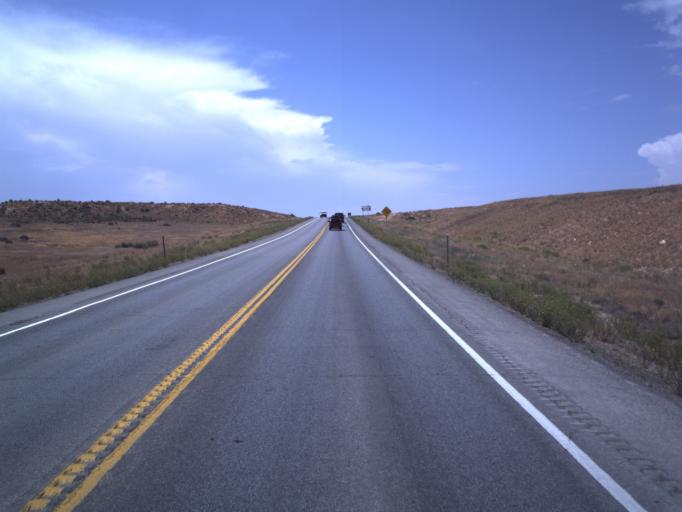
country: US
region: Utah
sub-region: Uintah County
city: Maeser
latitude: 40.3354
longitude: -109.6405
